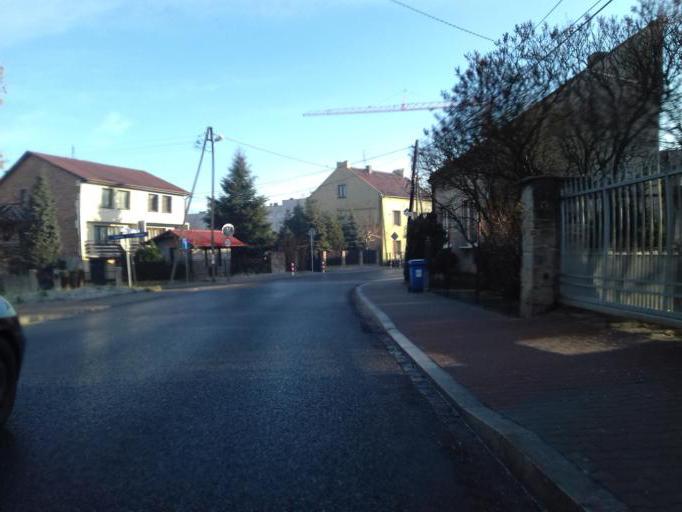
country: PL
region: Lesser Poland Voivodeship
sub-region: Krakow
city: Krakow
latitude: 50.0202
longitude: 19.9540
